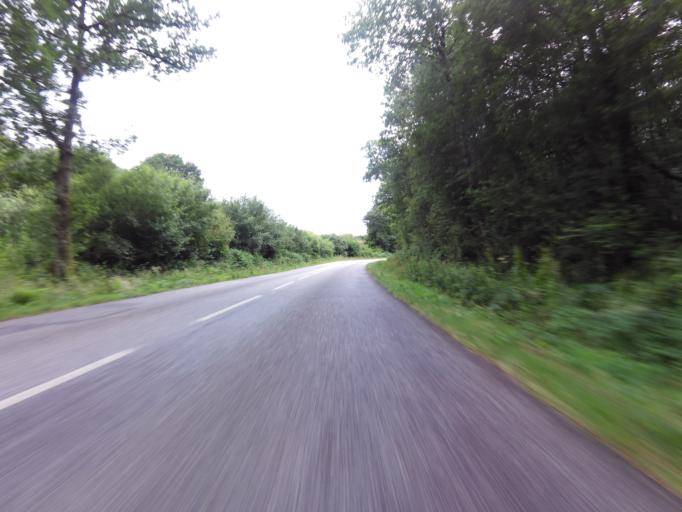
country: FR
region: Brittany
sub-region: Departement du Morbihan
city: Malansac
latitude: 47.7223
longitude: -2.3178
